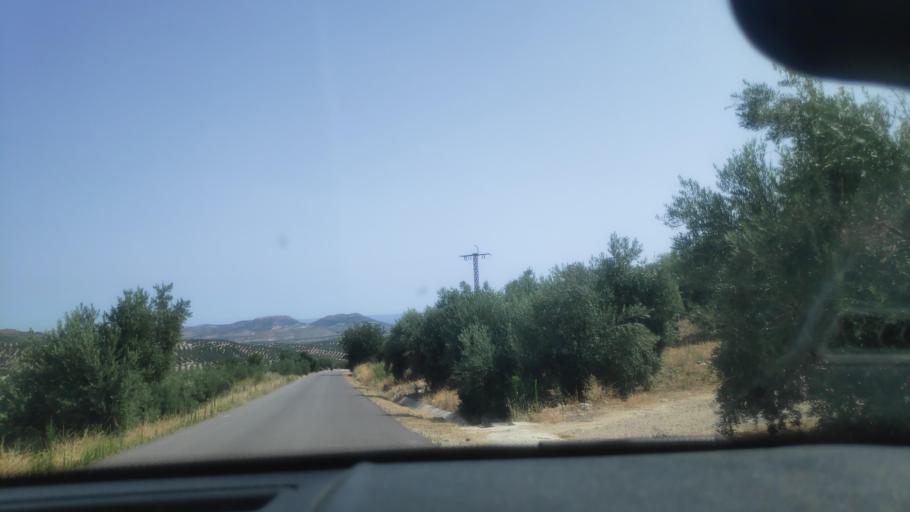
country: ES
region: Andalusia
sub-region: Provincia de Jaen
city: Jimena
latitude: 37.8005
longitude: -3.4458
